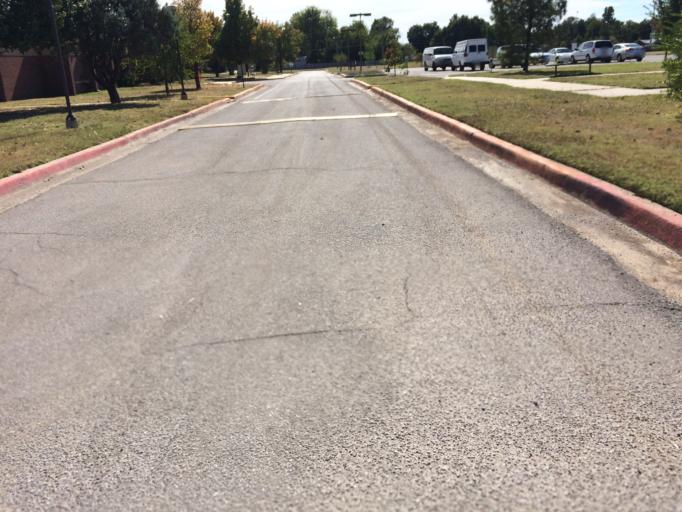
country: US
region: Oklahoma
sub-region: Cleveland County
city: Norman
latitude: 35.2200
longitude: -97.4282
